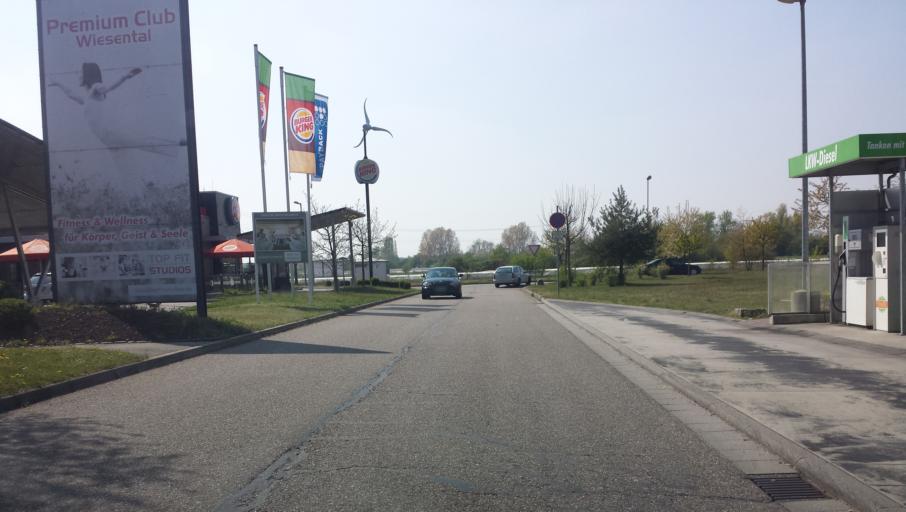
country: DE
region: Baden-Wuerttemberg
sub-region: Karlsruhe Region
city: Hambrucken
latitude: 49.2128
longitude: 8.5237
